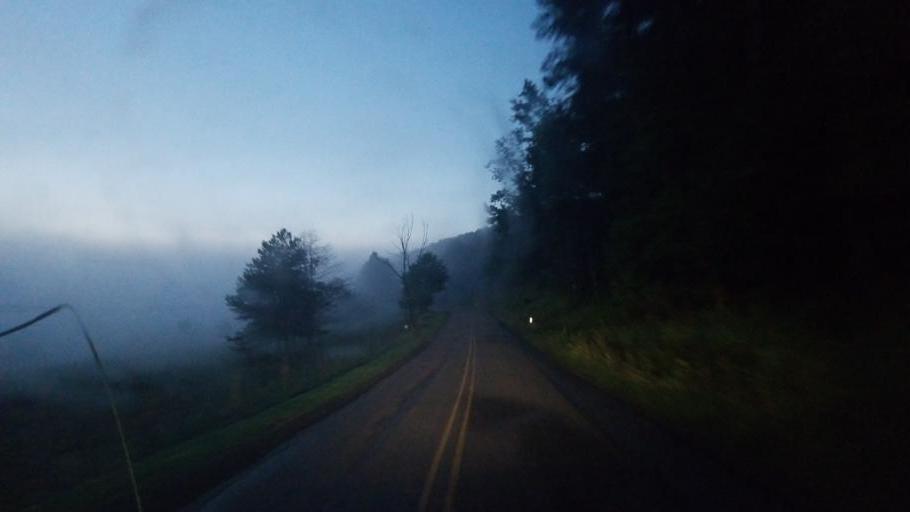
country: US
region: New York
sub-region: Allegany County
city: Wellsville
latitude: 41.9580
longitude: -77.8387
